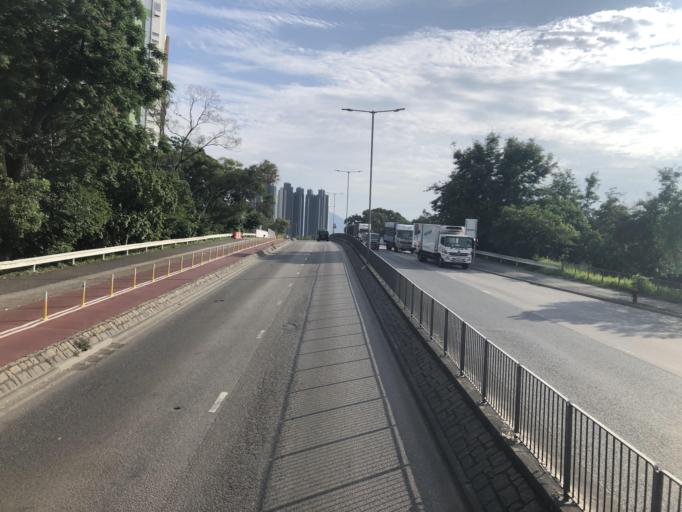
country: CN
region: Guangdong
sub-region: Shenzhen
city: Shenzhen
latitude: 22.5057
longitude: 114.1251
